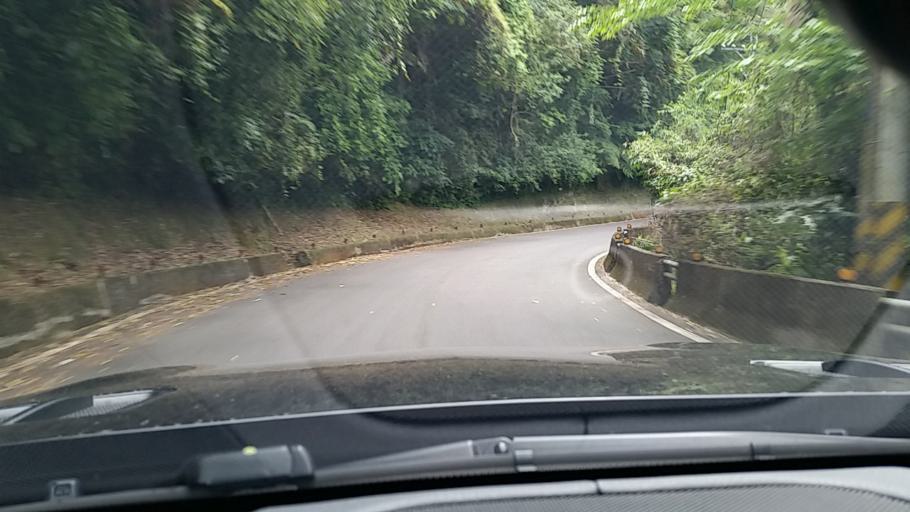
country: TW
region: Taiwan
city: Daxi
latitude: 24.7981
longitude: 121.3171
